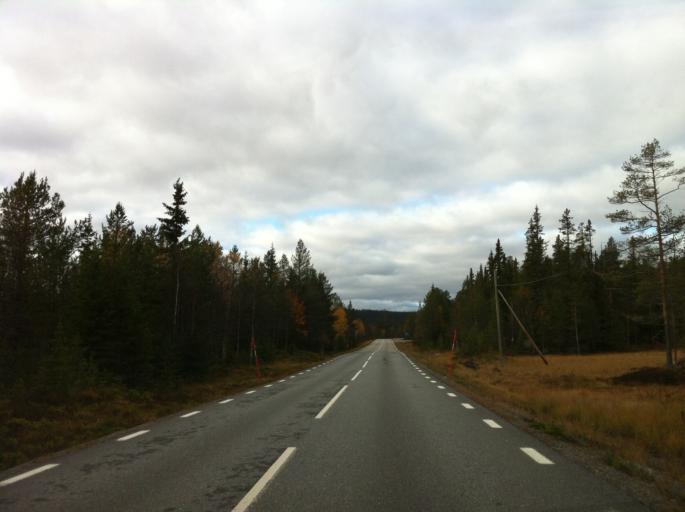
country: NO
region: Hedmark
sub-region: Engerdal
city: Engerdal
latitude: 62.0015
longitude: 12.4278
